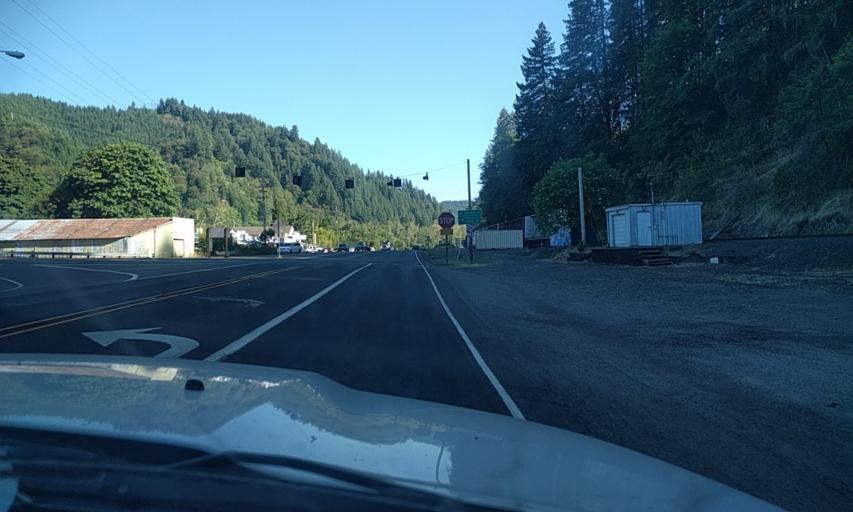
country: US
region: Oregon
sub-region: Lane County
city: Florence
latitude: 44.0317
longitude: -123.8599
